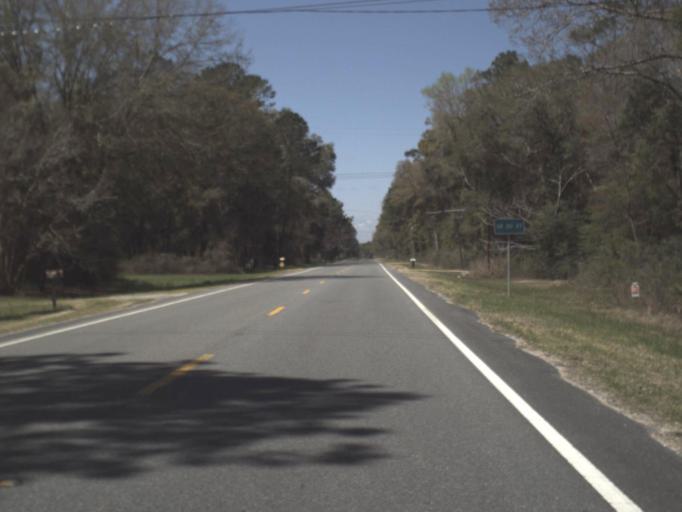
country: US
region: Florida
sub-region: Leon County
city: Woodville
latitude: 30.2332
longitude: -84.2345
